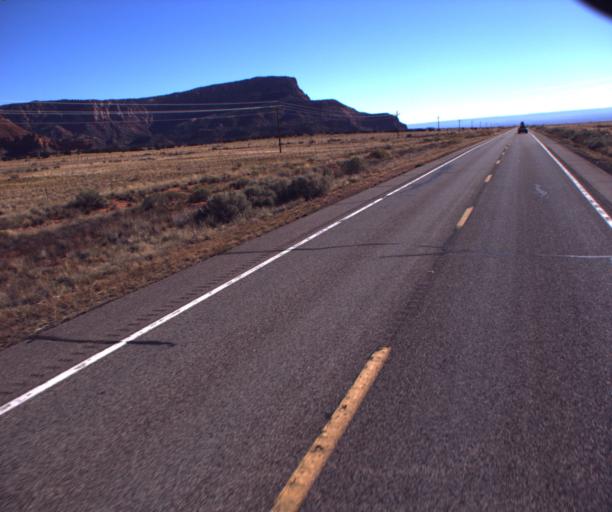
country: US
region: Arizona
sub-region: Mohave County
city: Colorado City
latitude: 36.8735
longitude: -112.8663
